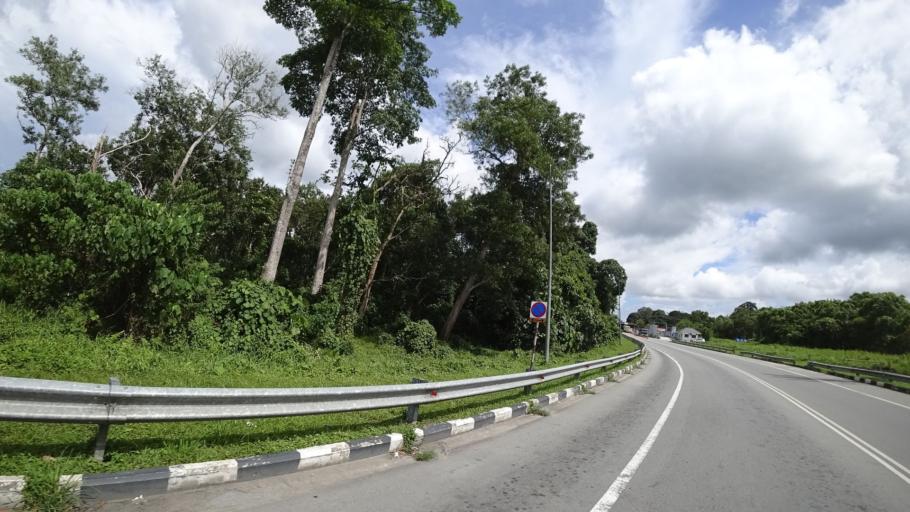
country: BN
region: Tutong
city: Tutong
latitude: 4.7432
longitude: 114.8141
